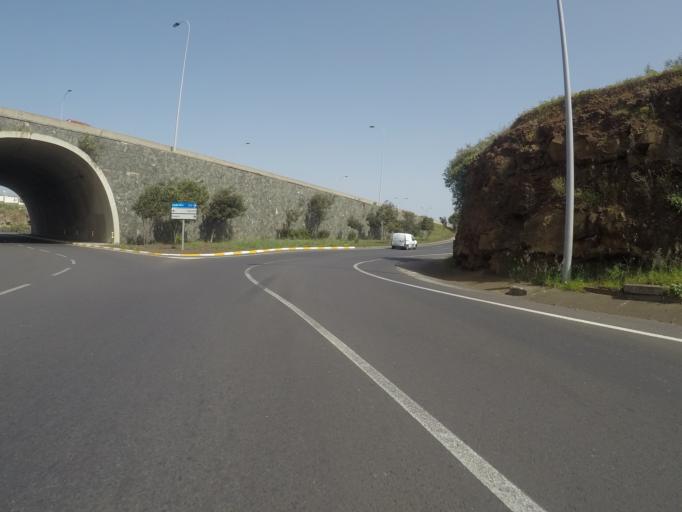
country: ES
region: Canary Islands
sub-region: Provincia de Santa Cruz de Tenerife
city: Tegueste
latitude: 28.5204
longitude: -16.2956
